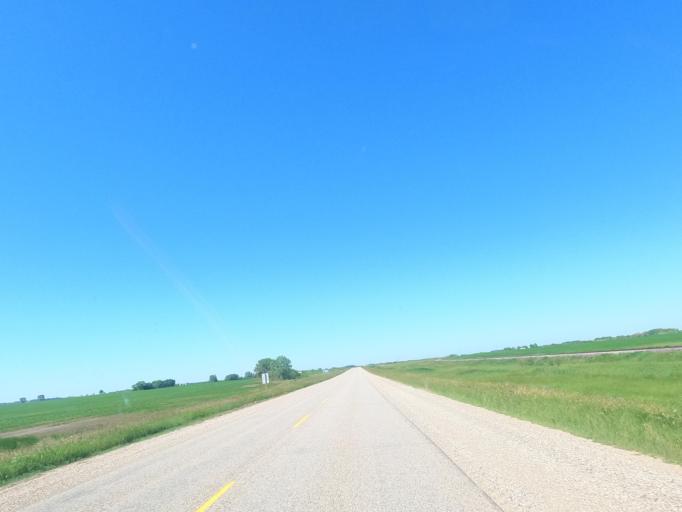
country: CA
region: Manitoba
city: Brandon
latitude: 49.5886
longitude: -99.9490
